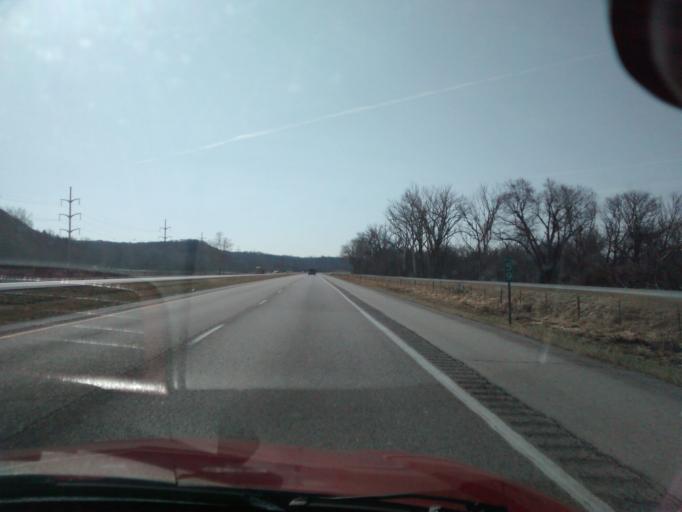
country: US
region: Iowa
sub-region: Pottawattamie County
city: Carter Lake
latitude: 41.3164
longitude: -95.8771
